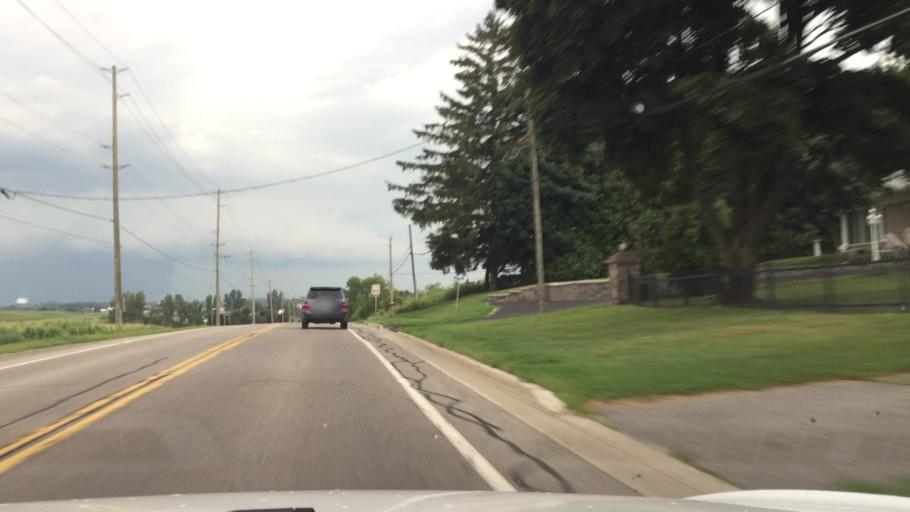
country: CA
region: Ontario
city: Oshawa
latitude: 43.9533
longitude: -78.8070
